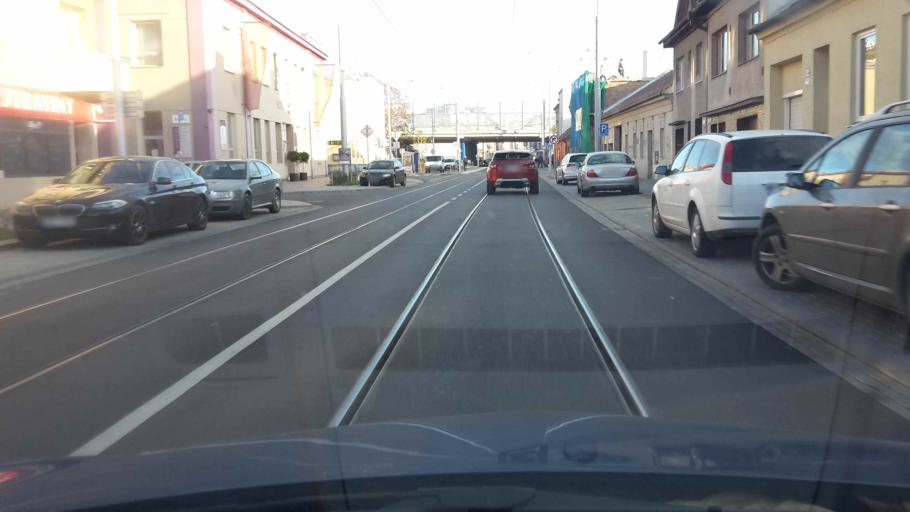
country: CZ
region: South Moravian
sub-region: Mesto Brno
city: Brno
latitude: 49.2140
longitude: 16.5735
